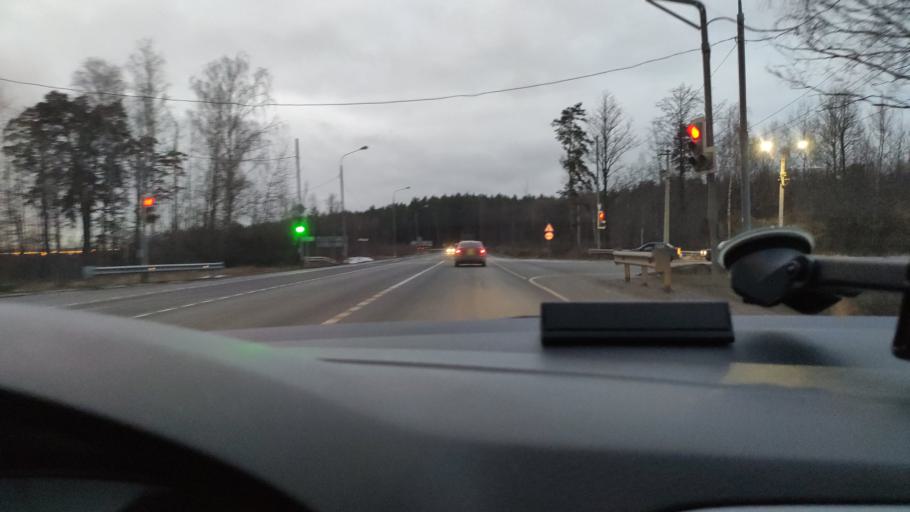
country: RU
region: Moskovskaya
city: Fryazevo
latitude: 55.7458
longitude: 38.4539
